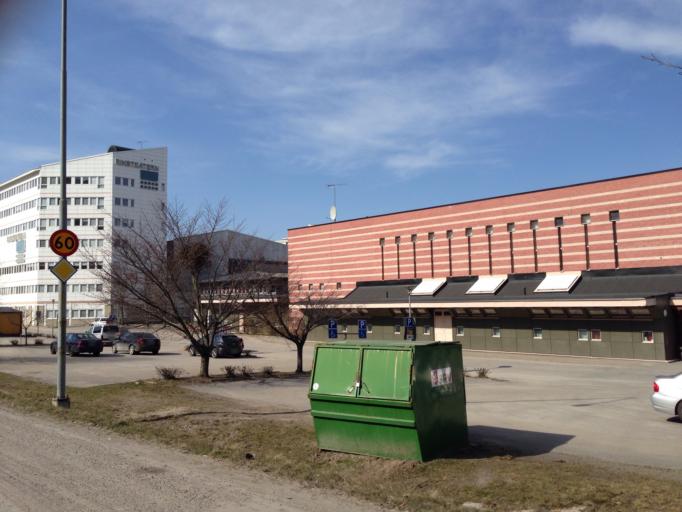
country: SE
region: Stockholm
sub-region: Botkyrka Kommun
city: Eriksberg
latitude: 59.2439
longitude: 17.8223
